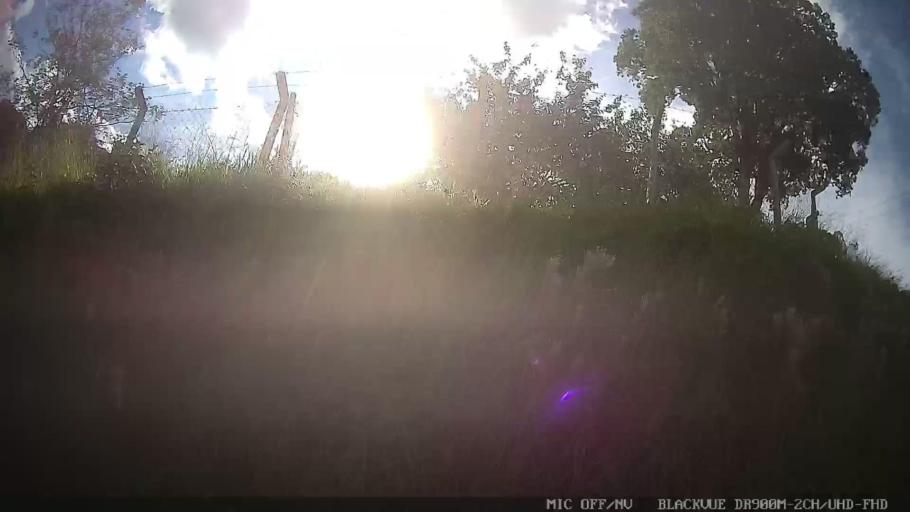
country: BR
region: Minas Gerais
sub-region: Extrema
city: Extrema
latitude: -22.8312
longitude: -46.2530
